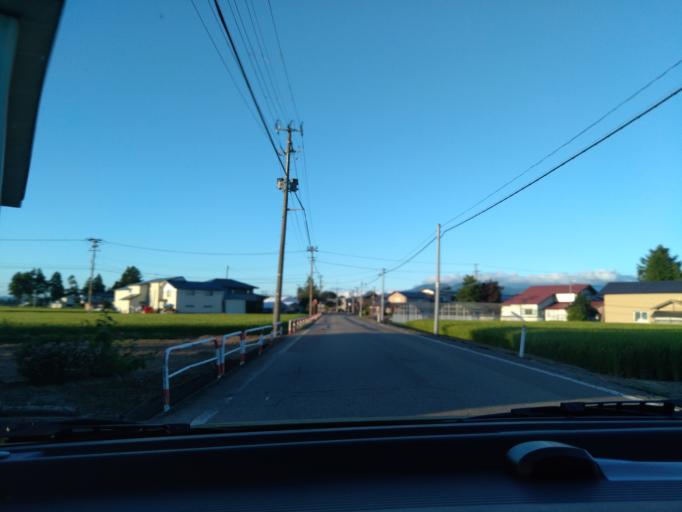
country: JP
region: Akita
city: Omagari
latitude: 39.4777
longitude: 140.5222
